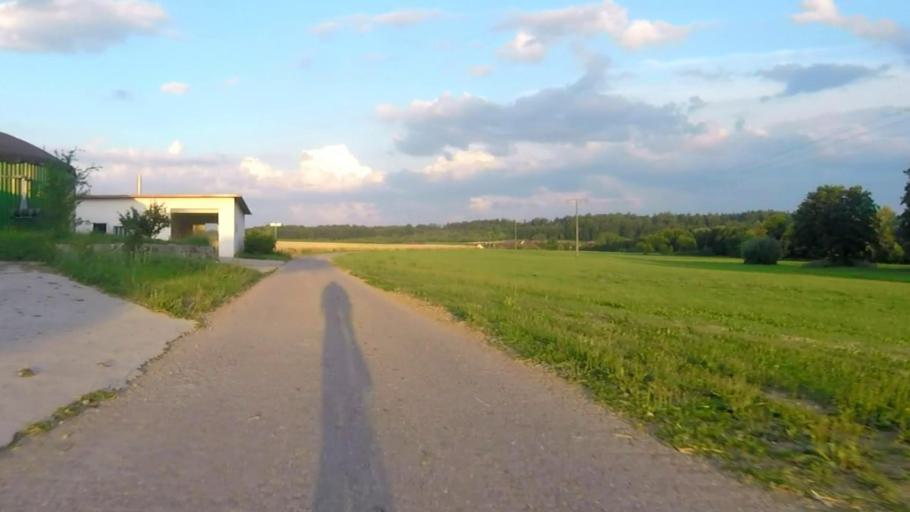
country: DE
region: Baden-Wuerttemberg
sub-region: Regierungsbezirk Stuttgart
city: Aspach
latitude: 48.9888
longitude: 9.3702
